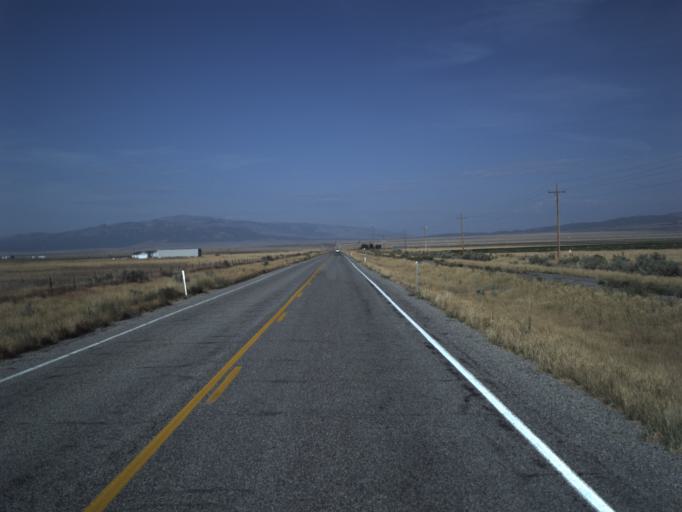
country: US
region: Idaho
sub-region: Oneida County
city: Malad City
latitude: 41.9666
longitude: -112.9040
